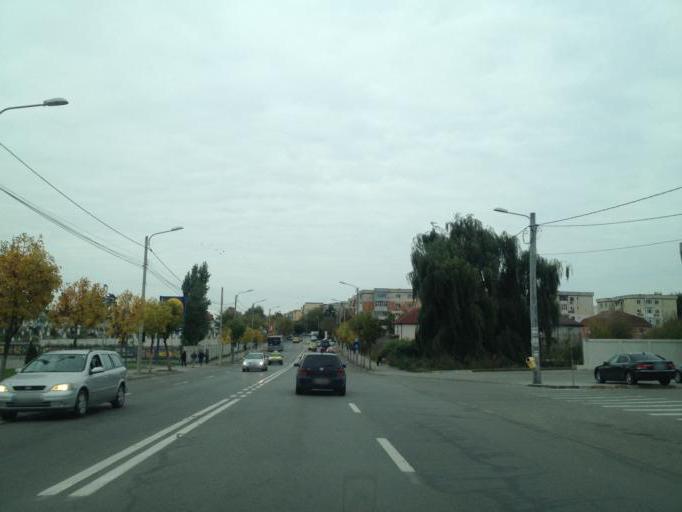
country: RO
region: Dolj
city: Craiova
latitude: 44.3319
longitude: 23.7822
